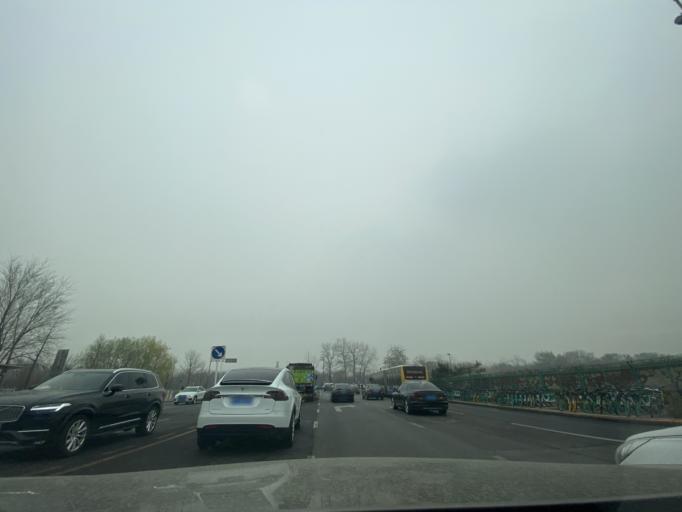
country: CN
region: Beijing
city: Sijiqing
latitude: 39.9721
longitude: 116.2552
